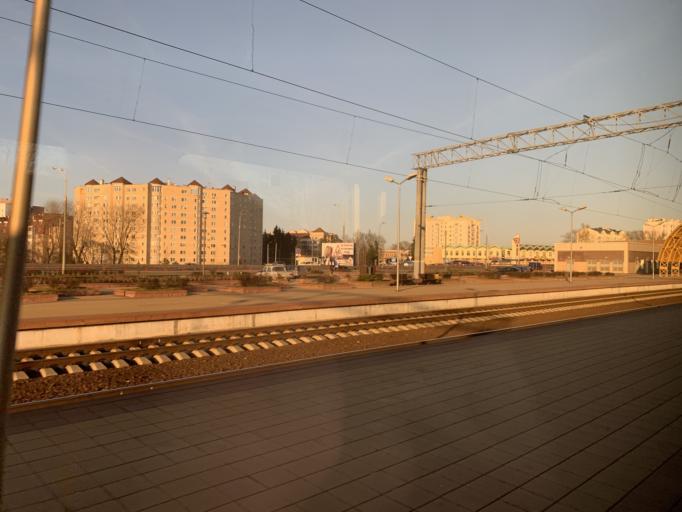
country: BY
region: Minsk
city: Zhdanovichy
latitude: 53.9477
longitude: 27.4245
